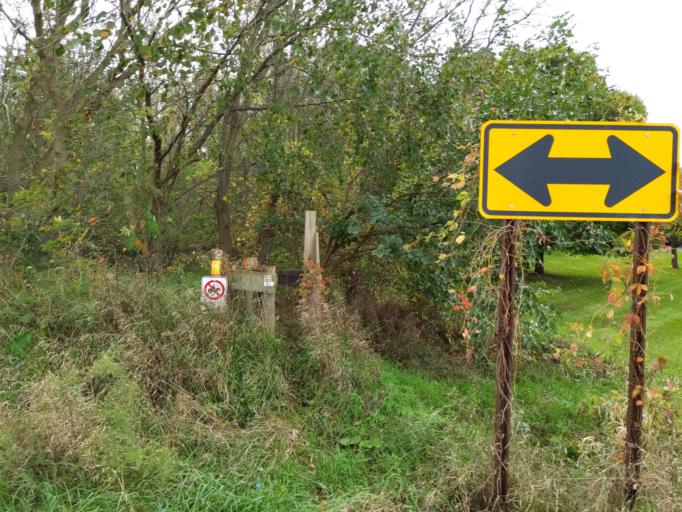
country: US
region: Michigan
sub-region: Eaton County
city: Potterville
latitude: 42.6545
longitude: -84.7586
